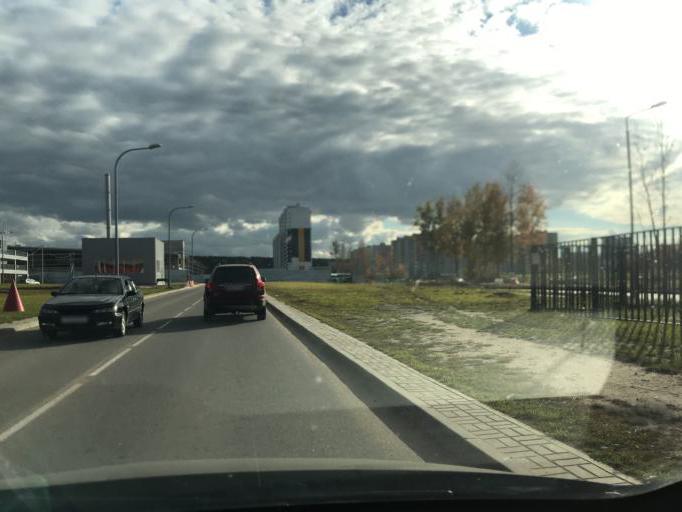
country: BY
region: Minsk
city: Borovlyany
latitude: 53.9350
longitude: 27.6729
